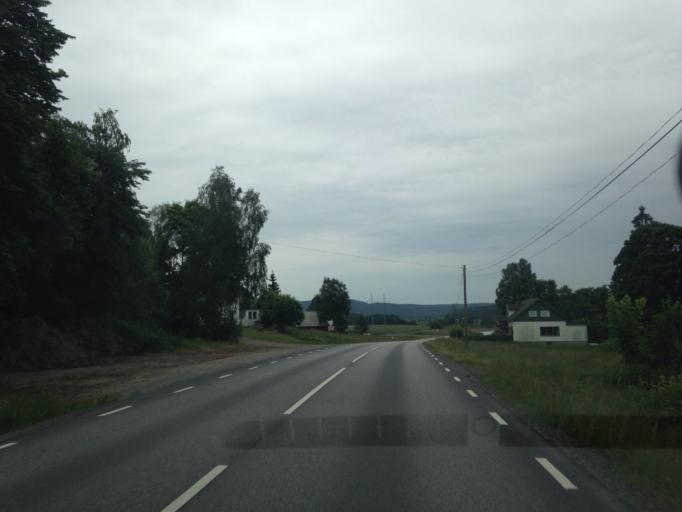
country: SE
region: Vaestra Goetaland
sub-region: Marks Kommun
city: Horred
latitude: 57.4794
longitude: 12.5174
